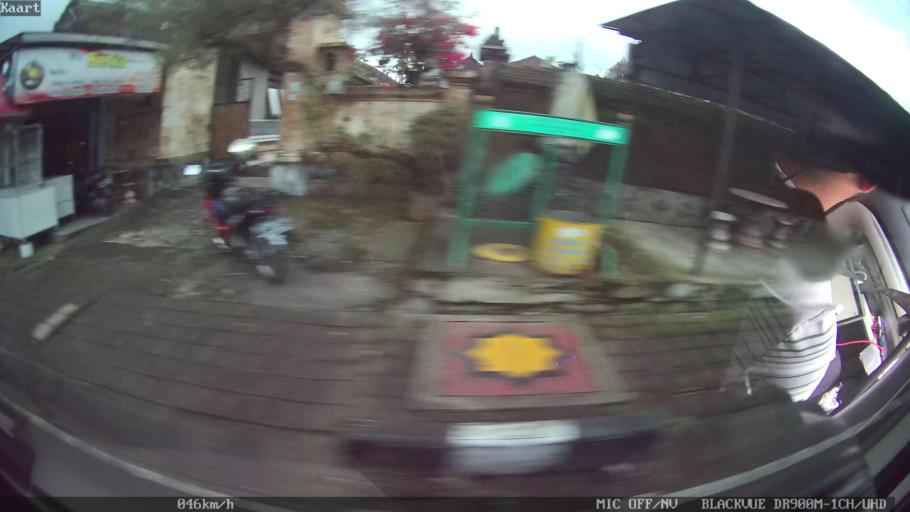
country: ID
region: Bali
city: Petang
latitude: -8.3937
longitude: 115.2188
